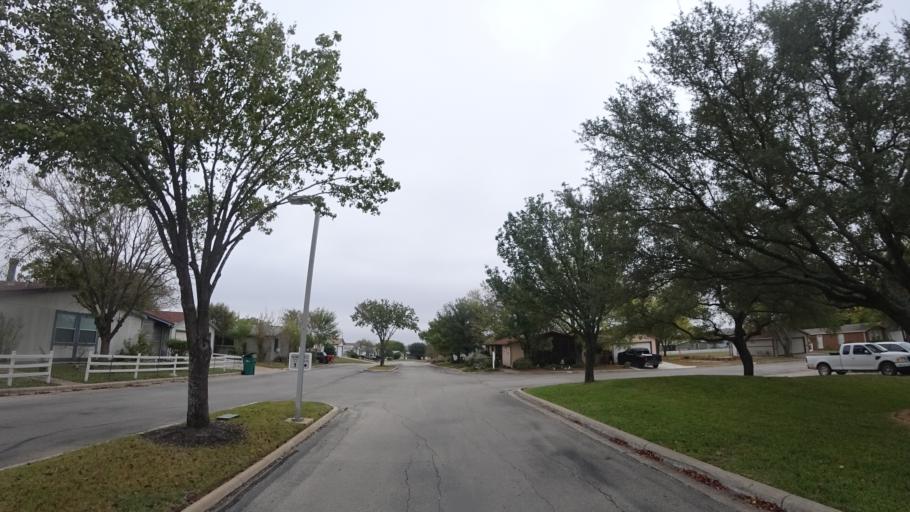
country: US
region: Texas
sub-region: Travis County
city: Pflugerville
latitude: 30.3910
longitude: -97.6422
